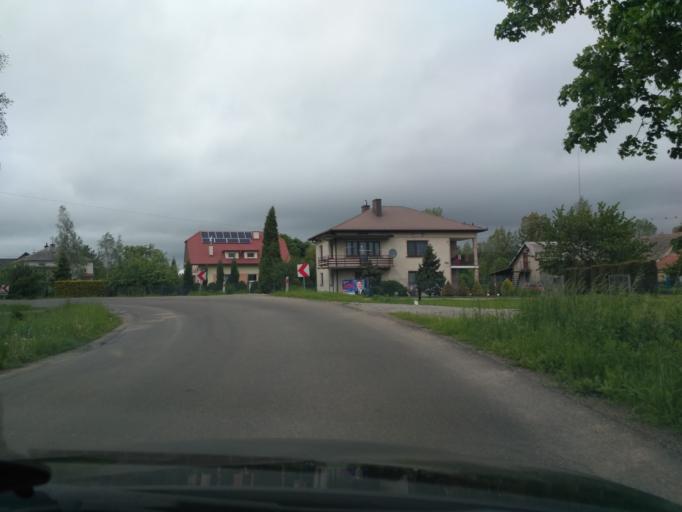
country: PL
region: Subcarpathian Voivodeship
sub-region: Powiat jasielski
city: Brzyska
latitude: 49.8211
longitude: 21.3961
